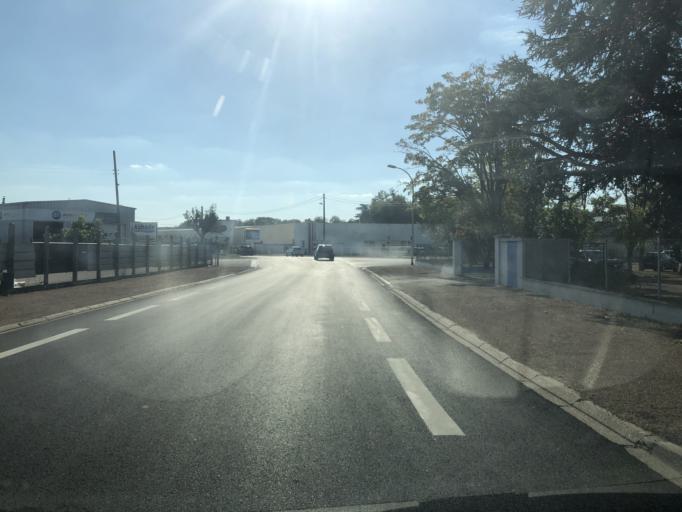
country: FR
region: Bourgogne
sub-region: Departement de l'Yonne
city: Auxerre
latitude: 47.8108
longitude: 3.5832
